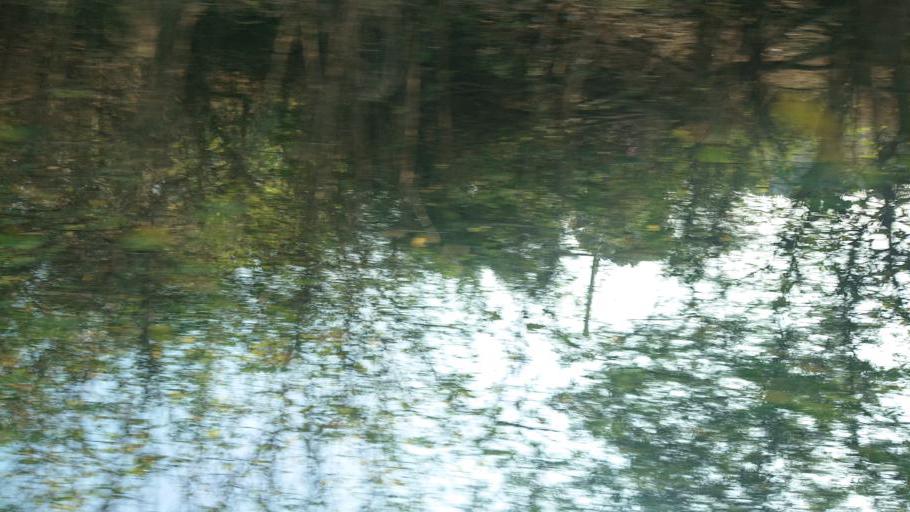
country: TW
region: Taiwan
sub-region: Tainan
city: Tainan
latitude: 23.1471
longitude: 120.2470
